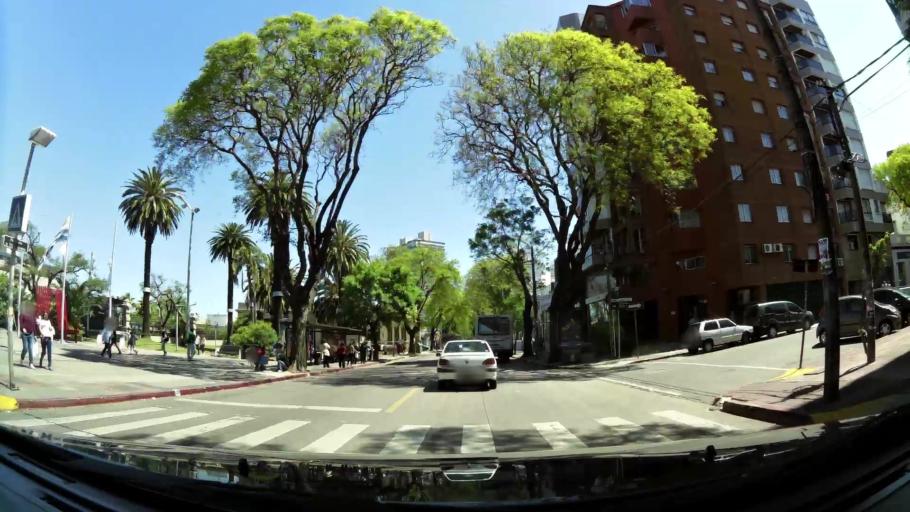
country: UY
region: Montevideo
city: Montevideo
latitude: -34.9234
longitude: -56.1597
